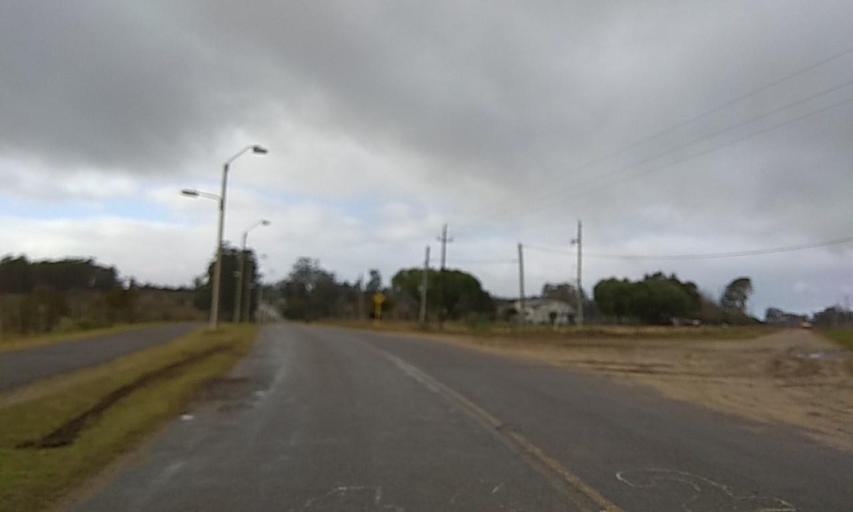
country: UY
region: Florida
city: Florida
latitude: -34.1142
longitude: -56.1958
